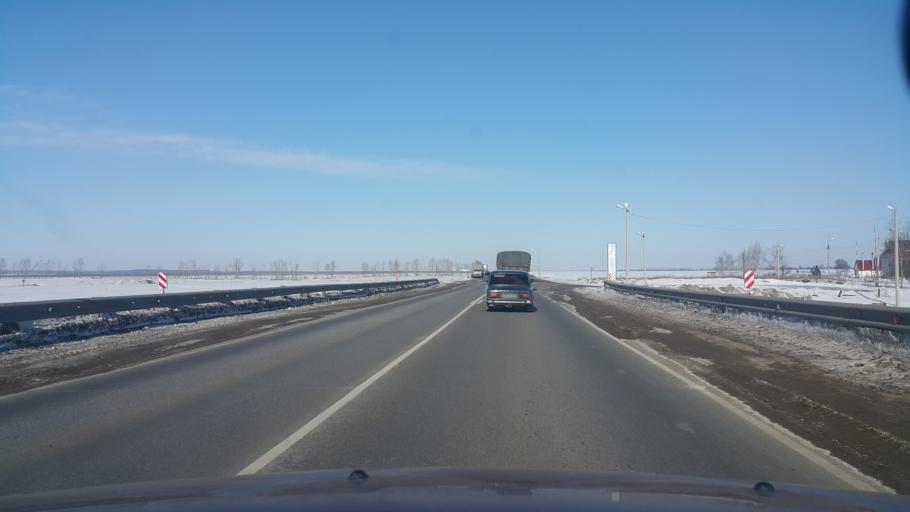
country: RU
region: Tambov
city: Pokrovo-Prigorodnoye
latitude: 52.6096
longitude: 41.3440
